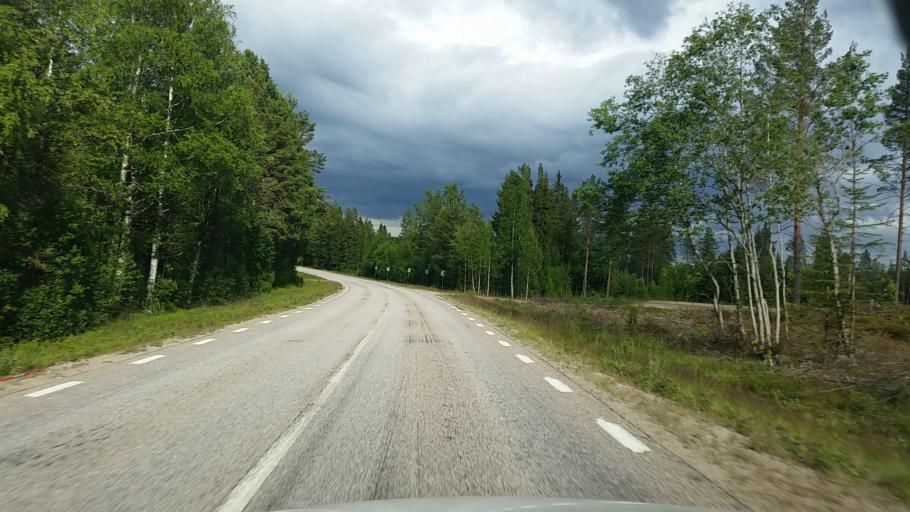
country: SE
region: Gaevleborg
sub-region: Ljusdals Kommun
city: Farila
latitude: 61.9788
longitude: 15.1150
